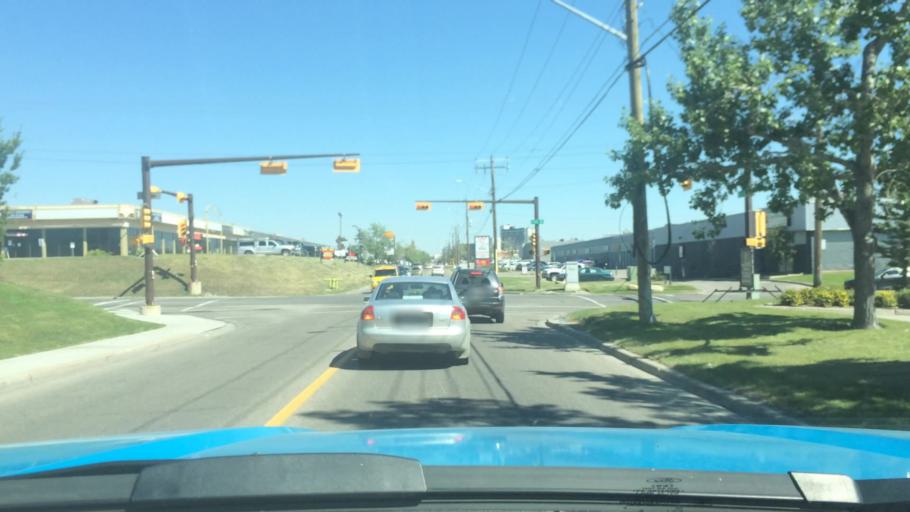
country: CA
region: Alberta
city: Calgary
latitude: 51.0566
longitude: -113.9860
